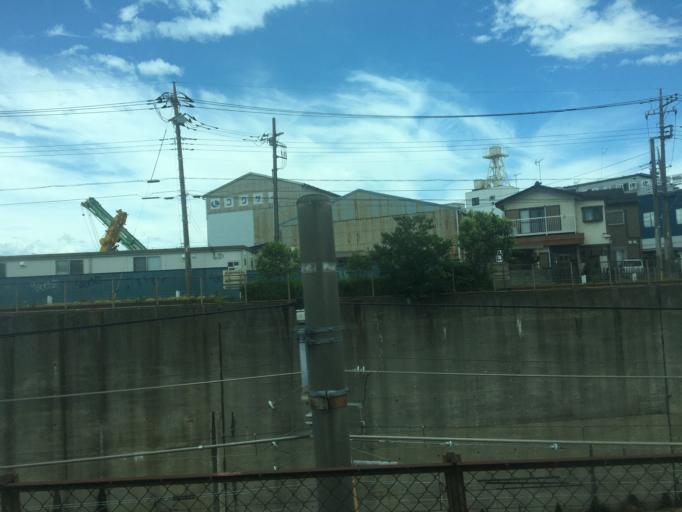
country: JP
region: Tokyo
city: Higashimurayama-shi
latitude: 35.7700
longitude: 139.4873
